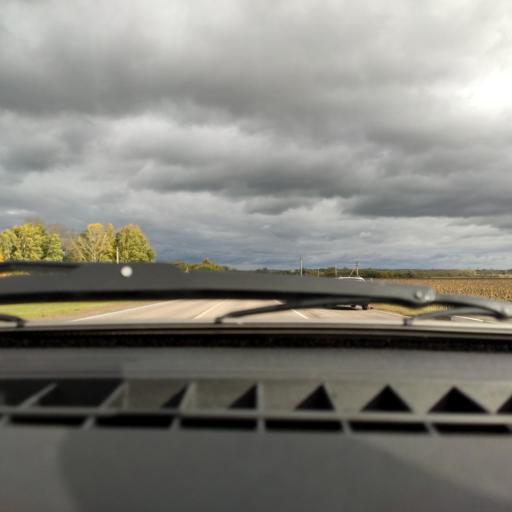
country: RU
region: Bashkortostan
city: Rayevskiy
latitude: 54.0136
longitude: 54.8655
